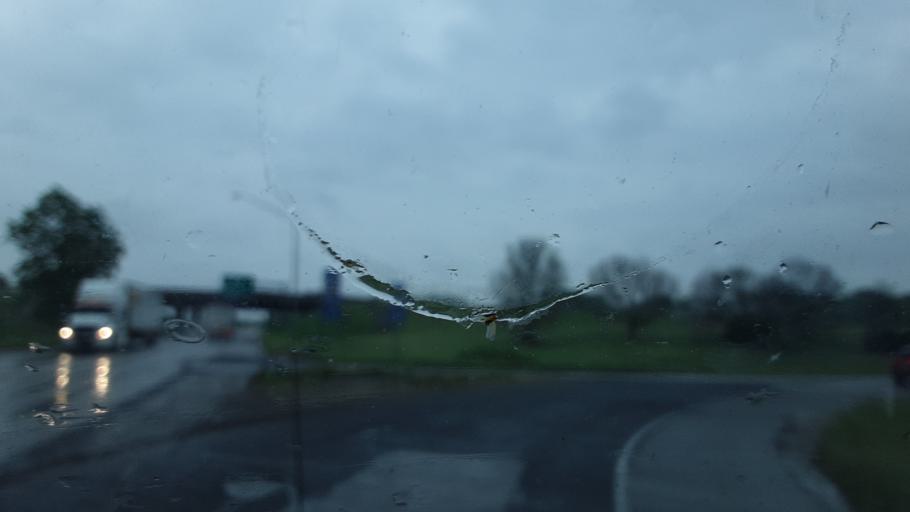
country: US
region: Indiana
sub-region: Steuben County
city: Fremont
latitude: 41.7478
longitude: -84.9981
